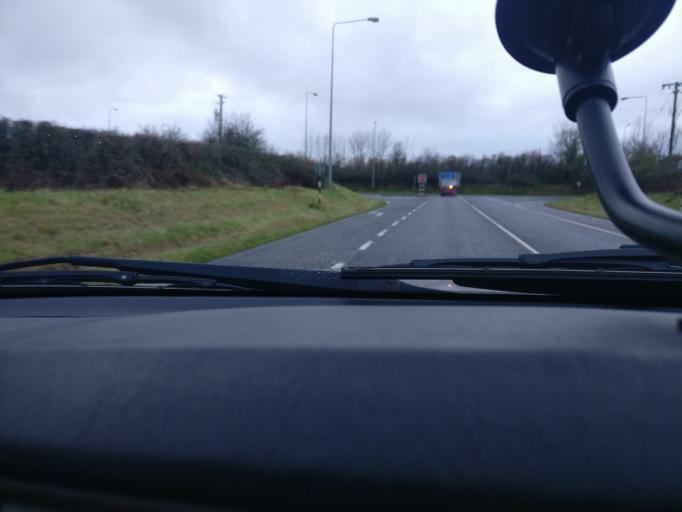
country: IE
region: Leinster
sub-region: Kildare
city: Kilcock
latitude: 53.4070
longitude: -6.6967
